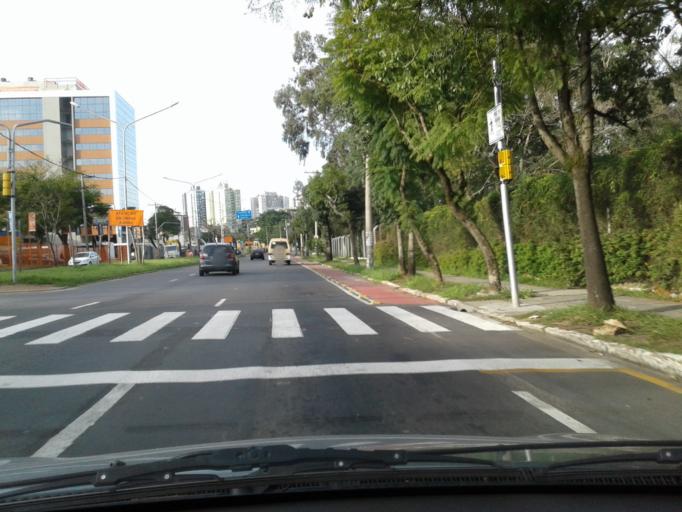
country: BR
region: Rio Grande do Sul
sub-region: Porto Alegre
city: Porto Alegre
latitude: -30.0955
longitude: -51.2455
